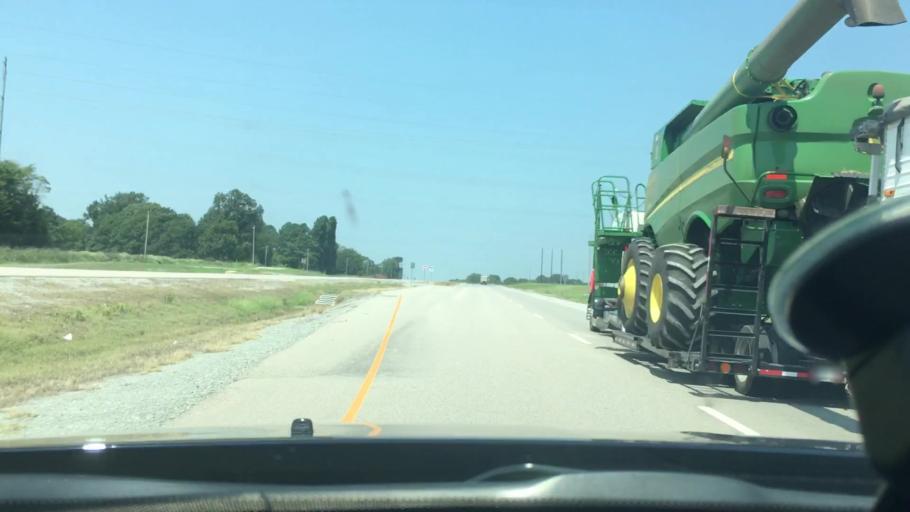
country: US
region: Oklahoma
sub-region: Atoka County
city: Atoka
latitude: 34.3299
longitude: -96.0488
